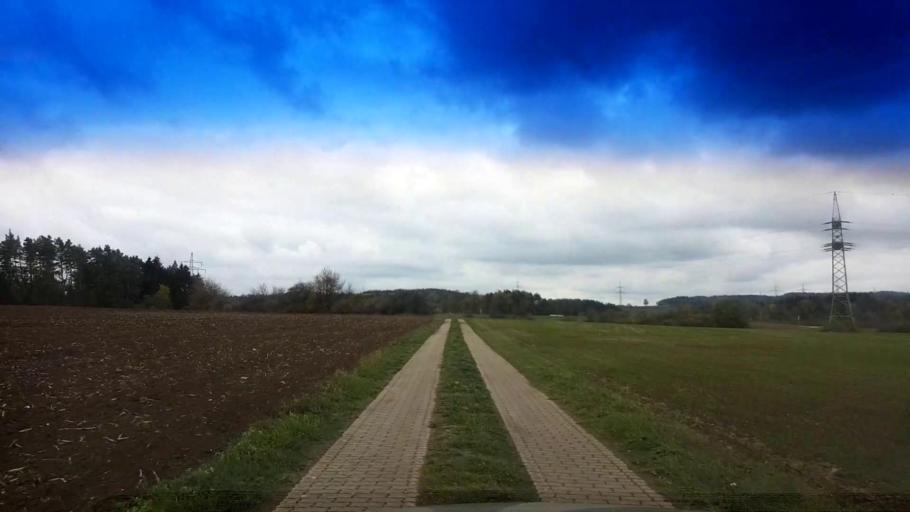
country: DE
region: Bavaria
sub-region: Upper Franconia
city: Poxdorf
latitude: 49.9795
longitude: 11.1187
